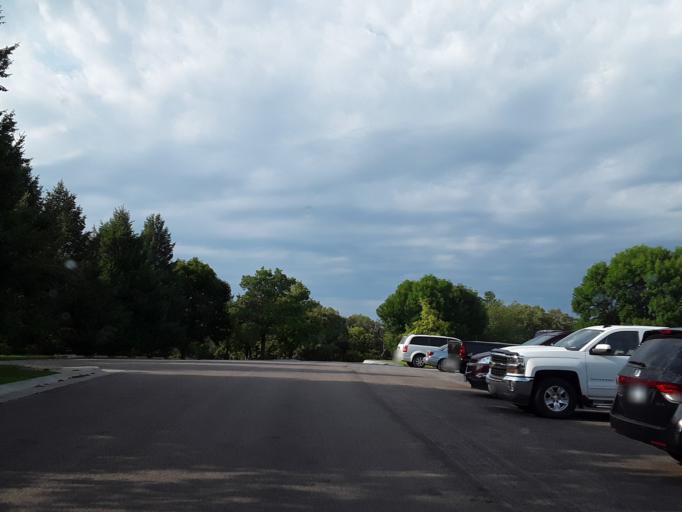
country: US
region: Nebraska
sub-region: Saunders County
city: Ashland
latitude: 41.0305
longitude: -96.3119
